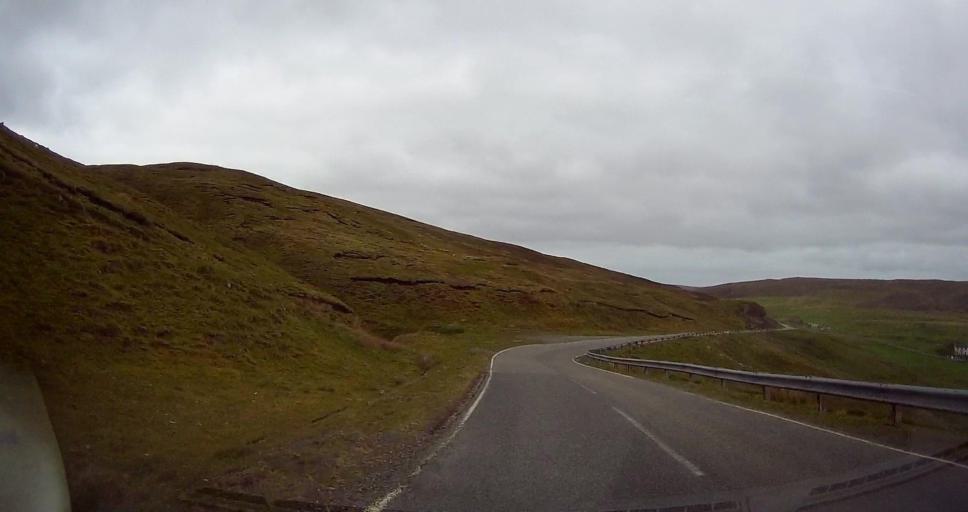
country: GB
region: Scotland
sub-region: Shetland Islands
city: Lerwick
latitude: 60.3422
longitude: -1.2878
